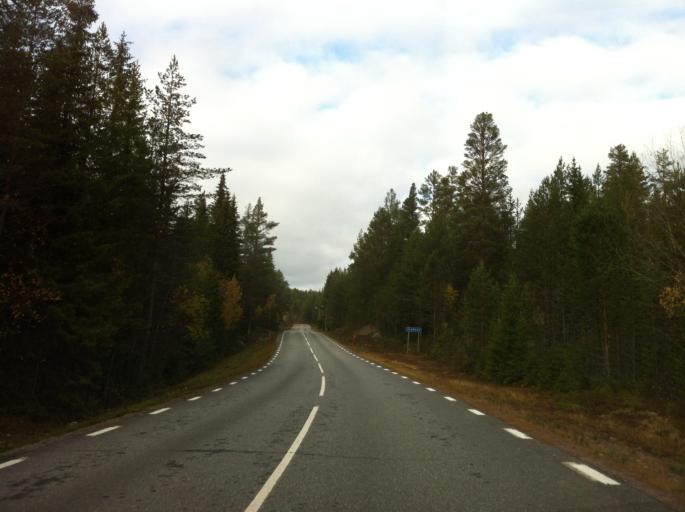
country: NO
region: Hedmark
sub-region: Engerdal
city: Engerdal
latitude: 61.9868
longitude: 12.4695
